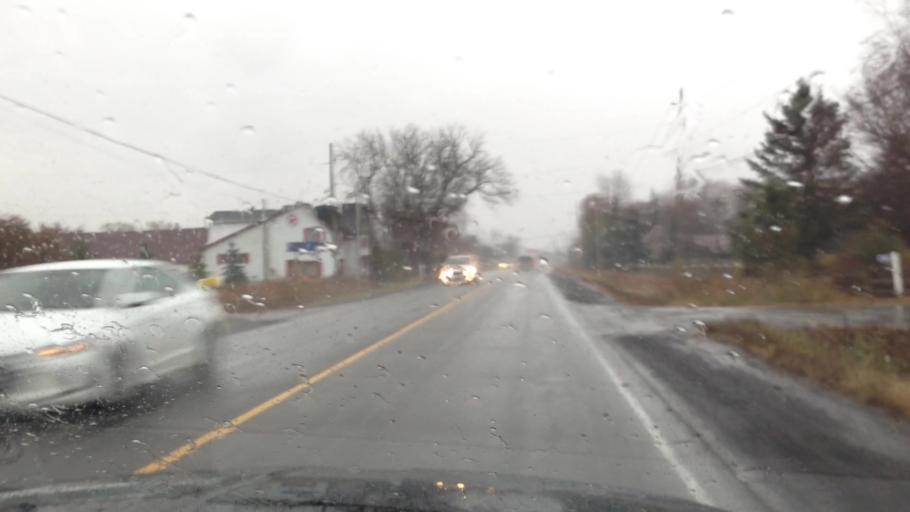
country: CA
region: Ontario
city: Bourget
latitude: 45.2994
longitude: -75.3279
